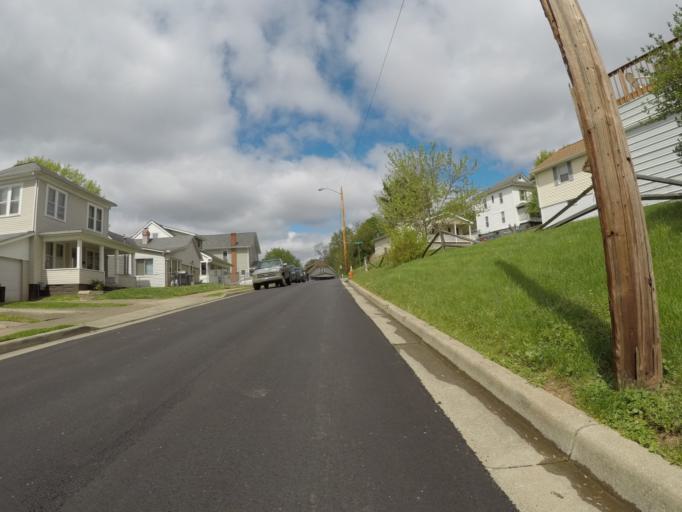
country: US
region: West Virginia
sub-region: Cabell County
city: Huntington
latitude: 38.4094
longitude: -82.4054
